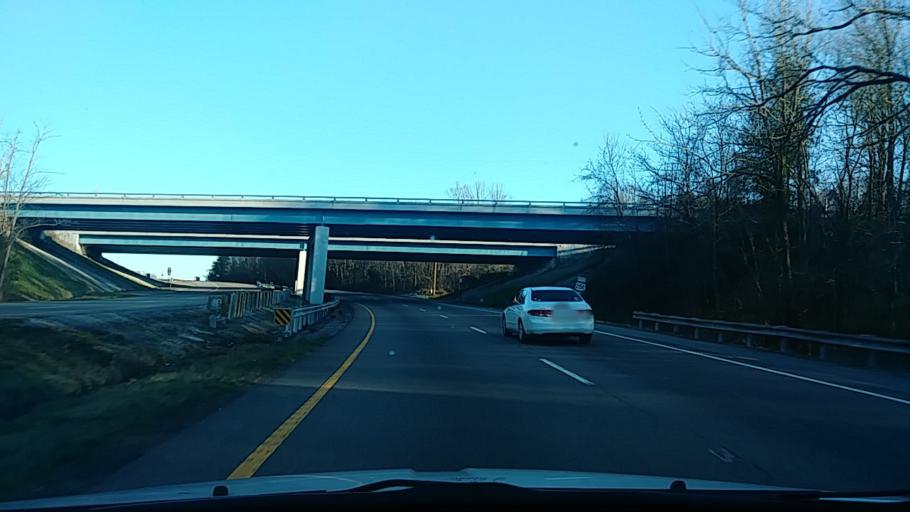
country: US
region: Tennessee
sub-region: Hamblen County
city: Morristown
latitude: 36.1917
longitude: -83.2693
